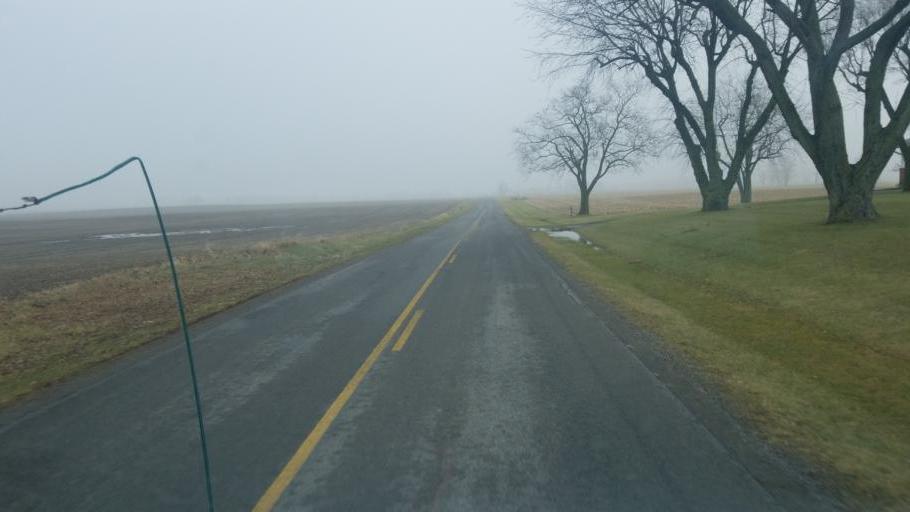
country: US
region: Ohio
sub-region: Hardin County
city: Kenton
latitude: 40.4908
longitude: -83.5432
